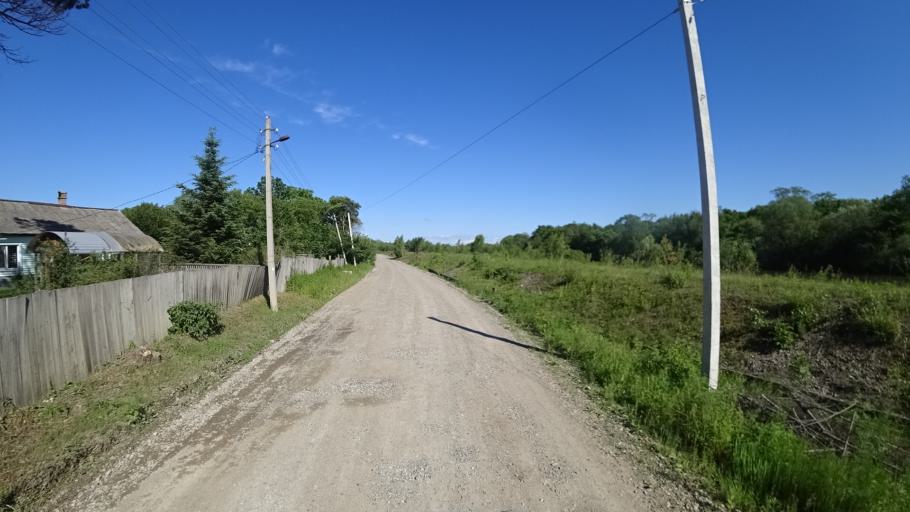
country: RU
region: Khabarovsk Krai
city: Khor
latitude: 47.8864
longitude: 135.0037
